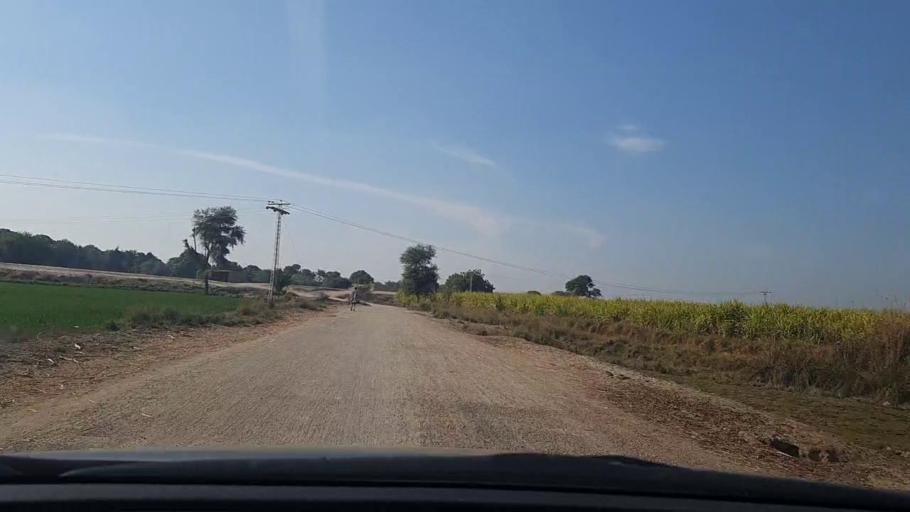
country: PK
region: Sindh
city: Sehwan
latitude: 26.3367
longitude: 67.9787
